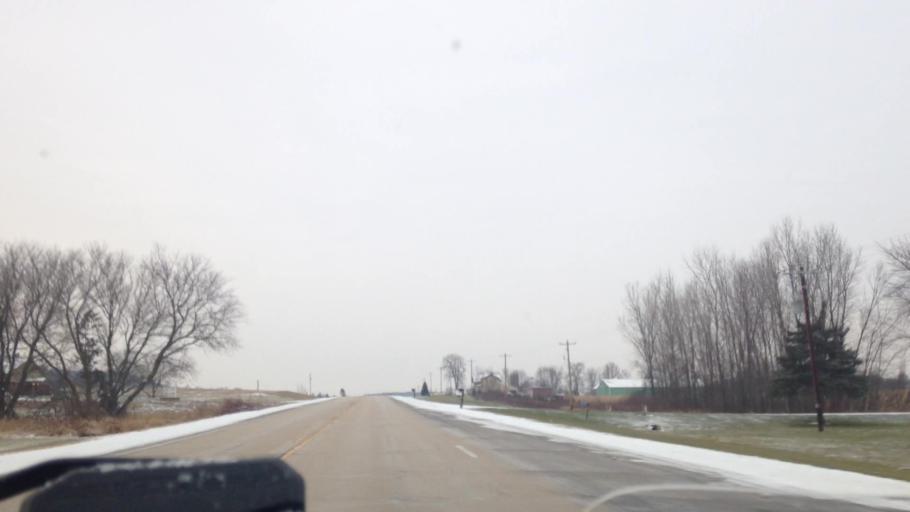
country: US
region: Wisconsin
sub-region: Dodge County
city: Mayville
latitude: 43.4793
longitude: -88.5460
